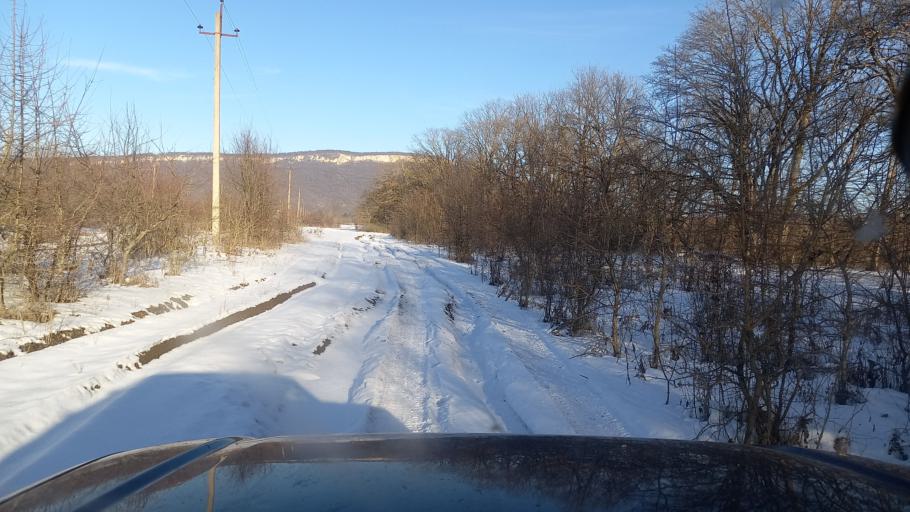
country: RU
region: Adygeya
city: Kamennomostskiy
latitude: 44.2159
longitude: 40.1741
